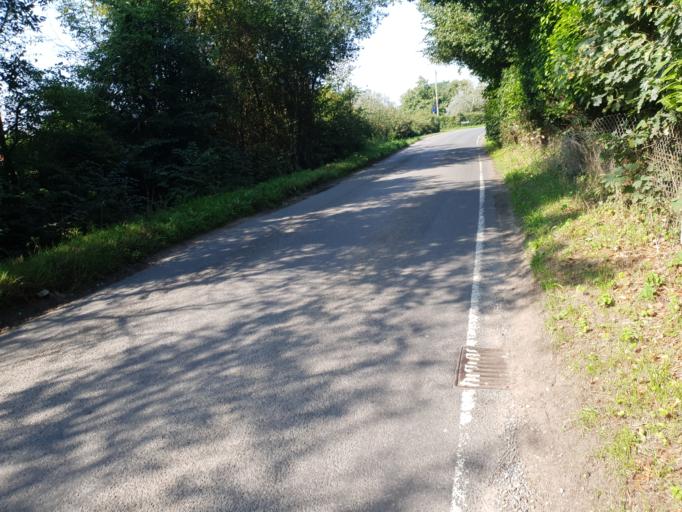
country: GB
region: England
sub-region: Suffolk
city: East Bergholt
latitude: 51.9364
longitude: 0.9935
